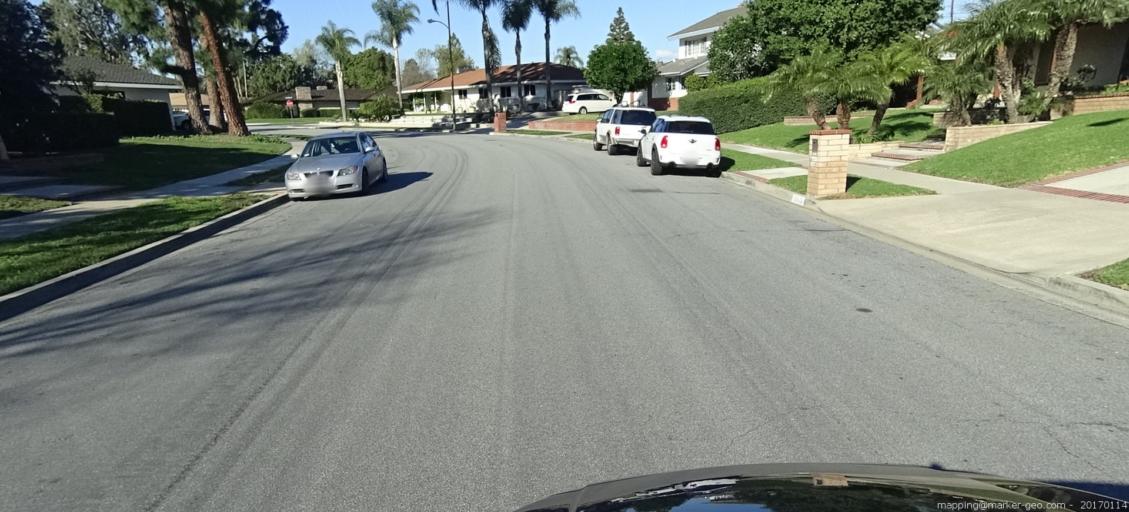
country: US
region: California
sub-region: Orange County
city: North Tustin
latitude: 33.7647
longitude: -117.8152
